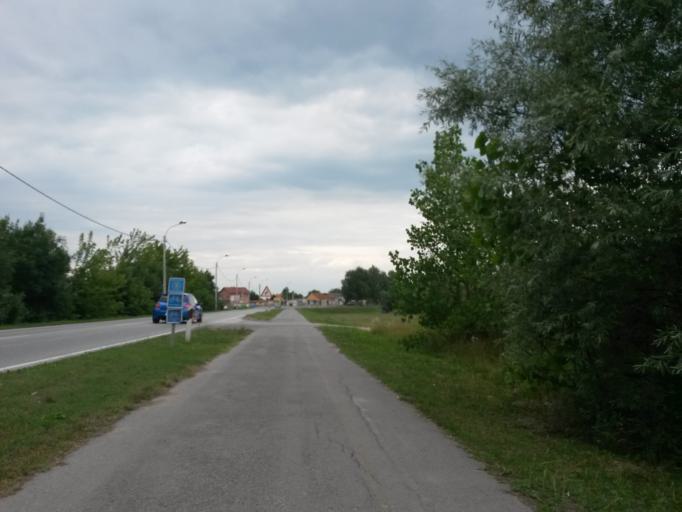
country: HR
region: Osjecko-Baranjska
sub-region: Grad Osijek
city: Bilje
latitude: 45.5928
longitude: 18.7386
